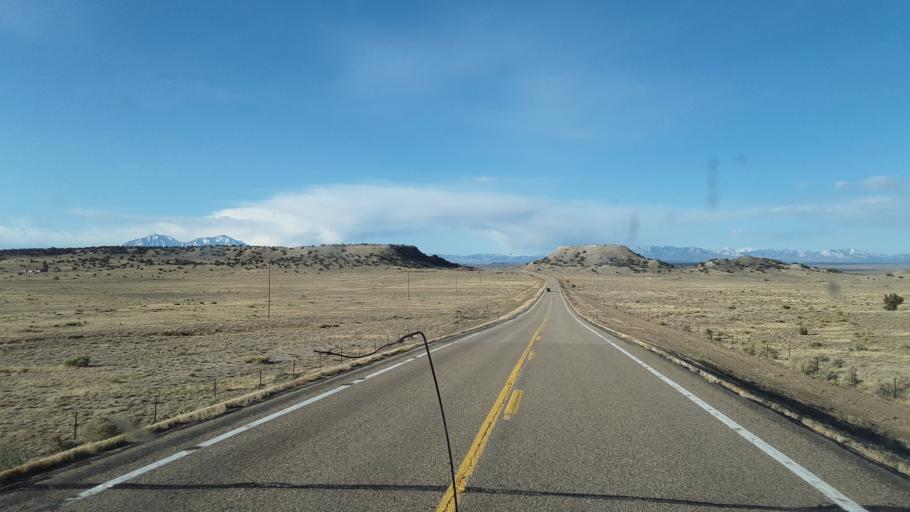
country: US
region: Colorado
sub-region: Huerfano County
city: Walsenburg
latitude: 37.6968
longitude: -104.6190
